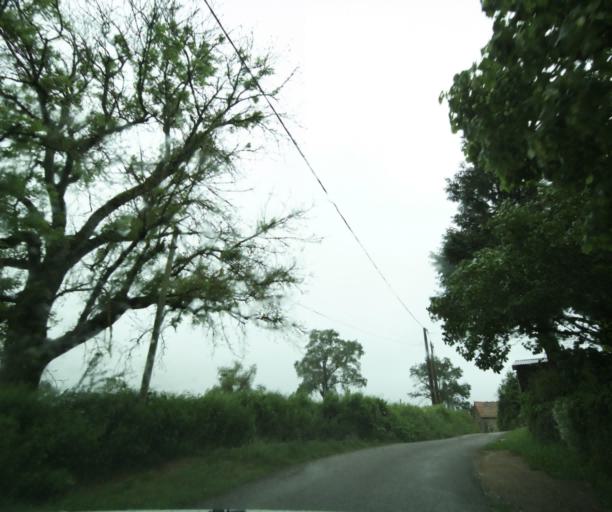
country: FR
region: Bourgogne
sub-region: Departement de Saone-et-Loire
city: Charolles
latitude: 46.3850
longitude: 4.3523
